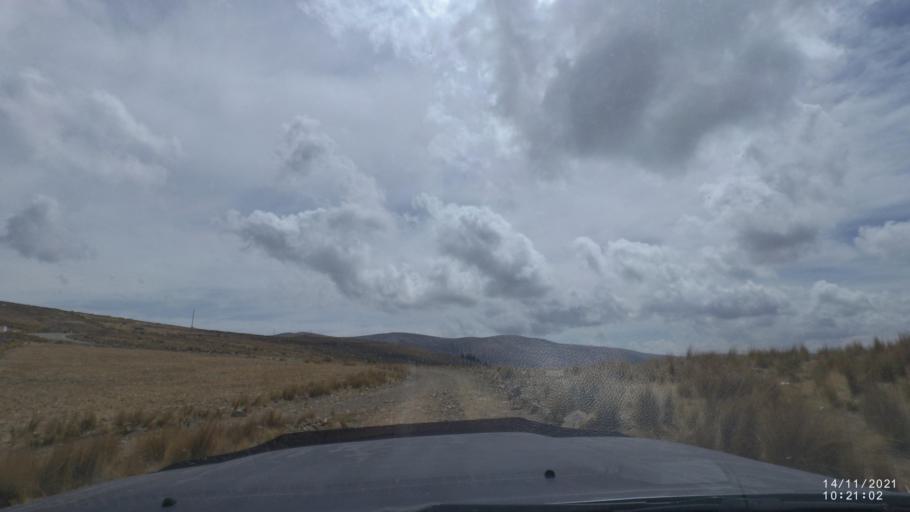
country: BO
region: Cochabamba
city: Cochabamba
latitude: -17.3339
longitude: -66.0803
